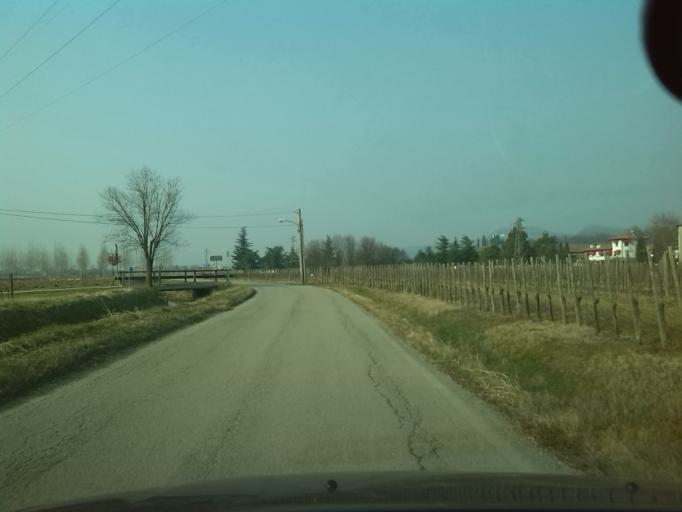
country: IT
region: Friuli Venezia Giulia
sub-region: Provincia di Gorizia
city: Moraro
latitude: 45.9334
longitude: 13.4794
